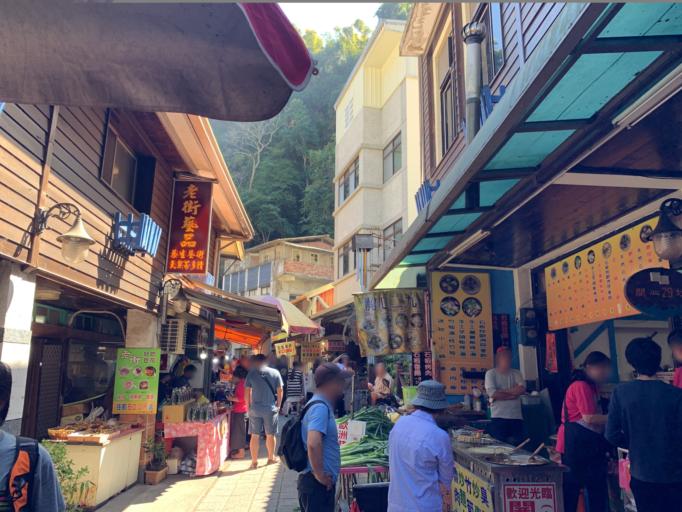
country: TW
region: Taiwan
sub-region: Miaoli
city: Miaoli
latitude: 24.4464
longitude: 120.9055
